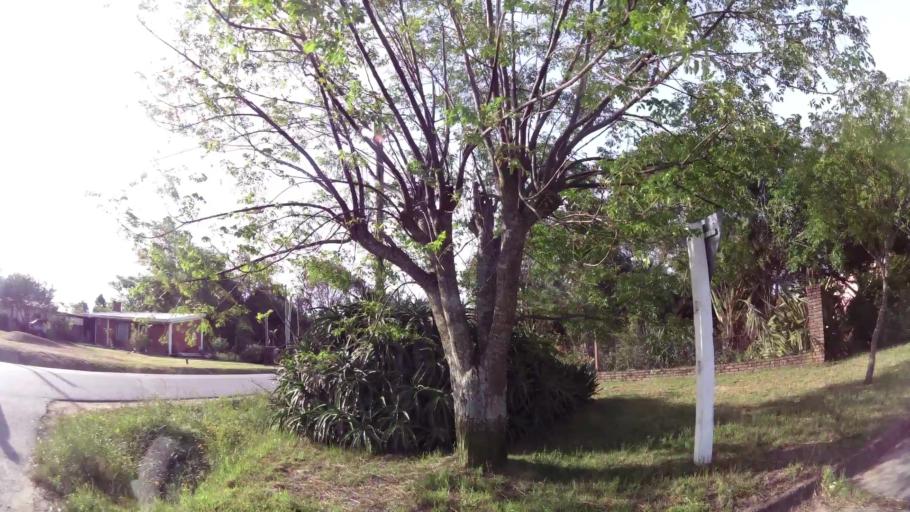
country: UY
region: Canelones
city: Atlantida
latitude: -34.7855
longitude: -55.8463
